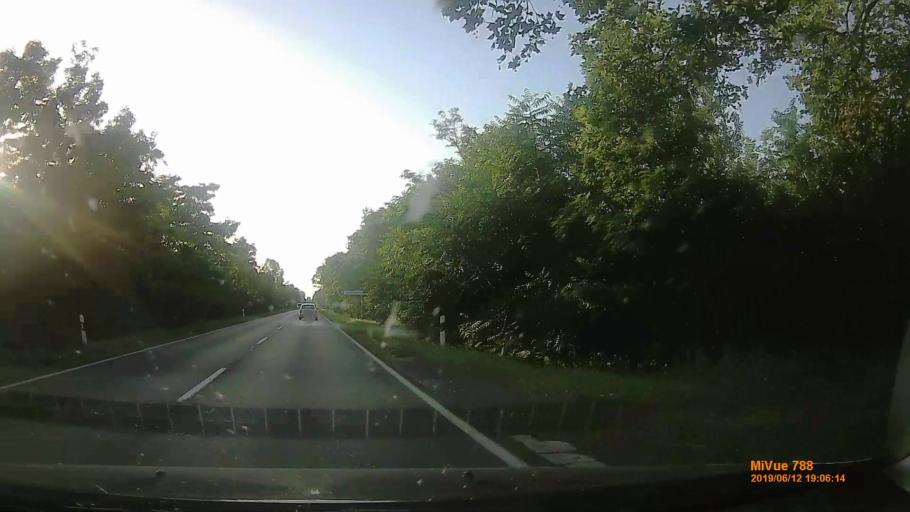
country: HU
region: Bacs-Kiskun
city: Varosfoeld
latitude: 46.7833
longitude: 19.7954
